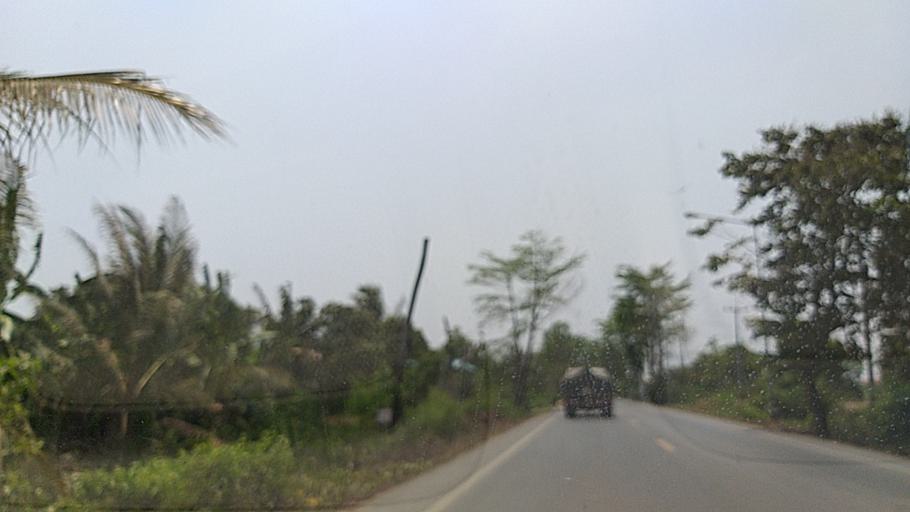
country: TH
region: Chachoengsao
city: Bang Nam Priao
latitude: 13.9126
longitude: 100.9741
